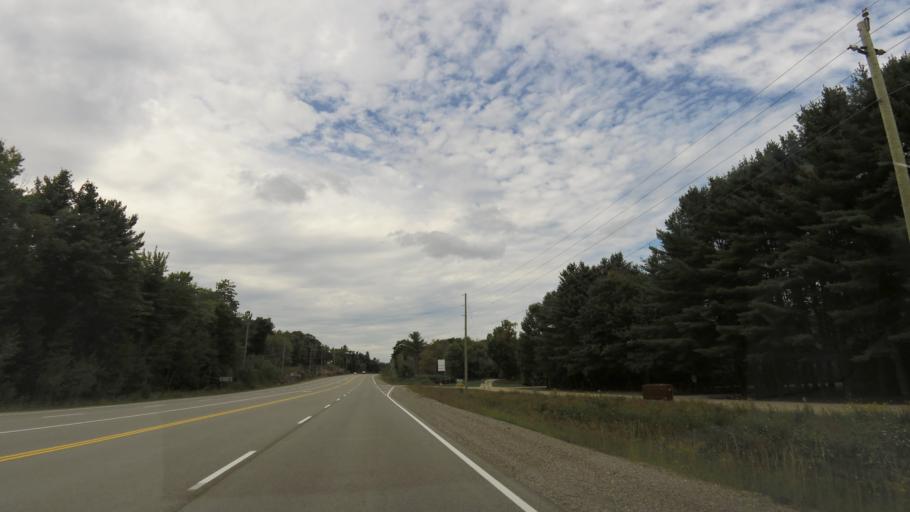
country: CA
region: Ontario
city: Omemee
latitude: 44.7891
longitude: -78.8117
